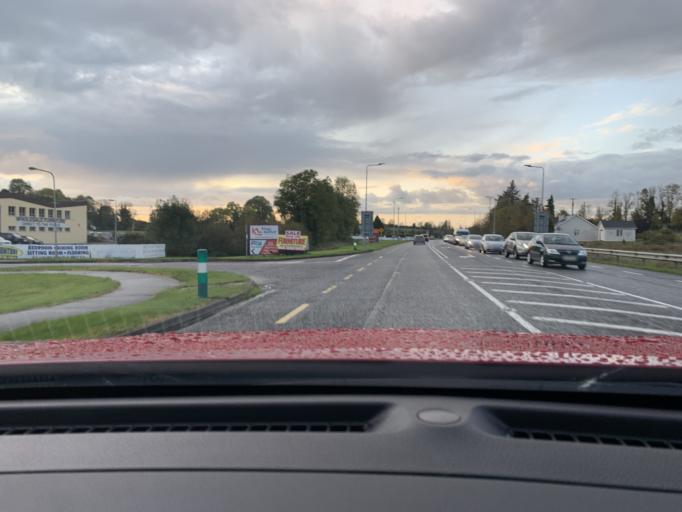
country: IE
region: Connaught
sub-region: County Leitrim
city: Carrick-on-Shannon
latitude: 53.9436
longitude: -8.1125
